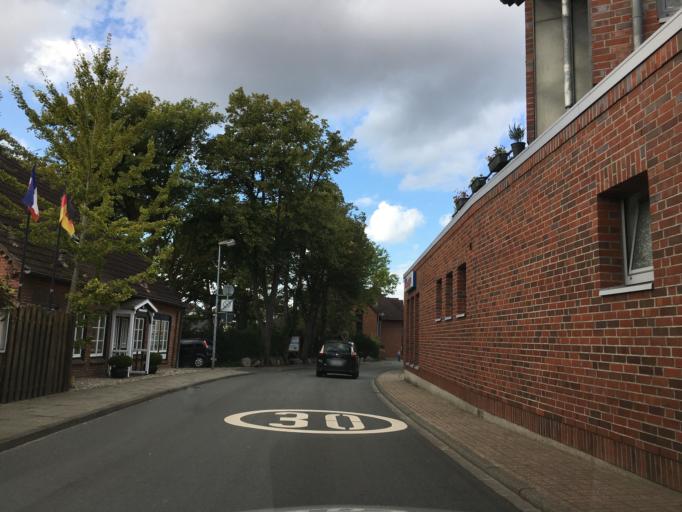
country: DE
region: Schleswig-Holstein
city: Krokau
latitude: 54.3926
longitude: 10.3721
